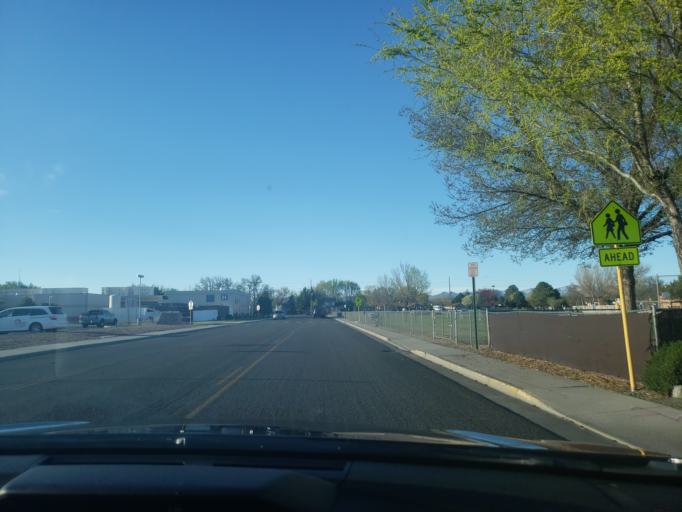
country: US
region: Colorado
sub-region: Mesa County
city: Fruita
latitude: 39.1624
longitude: -108.7359
